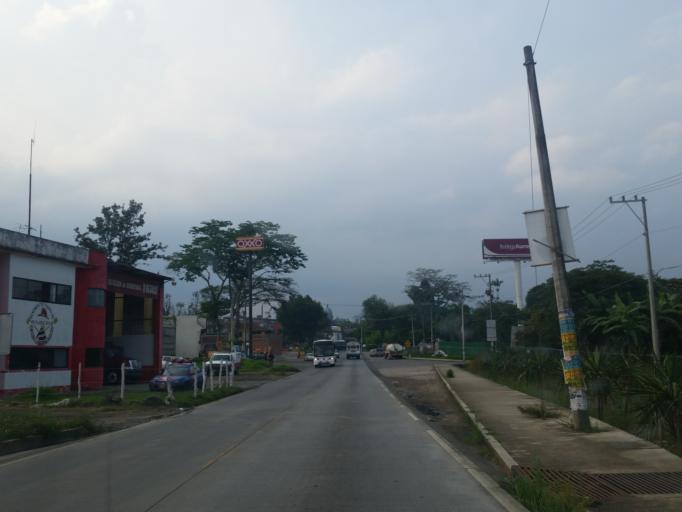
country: MX
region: Veracruz
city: Coatepec
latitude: 19.4476
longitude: -96.9537
